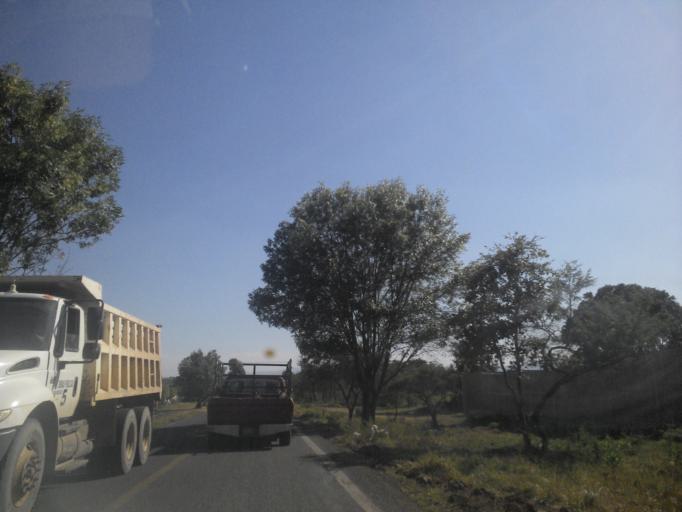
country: MX
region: Jalisco
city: Arandas
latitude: 20.7380
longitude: -102.3181
